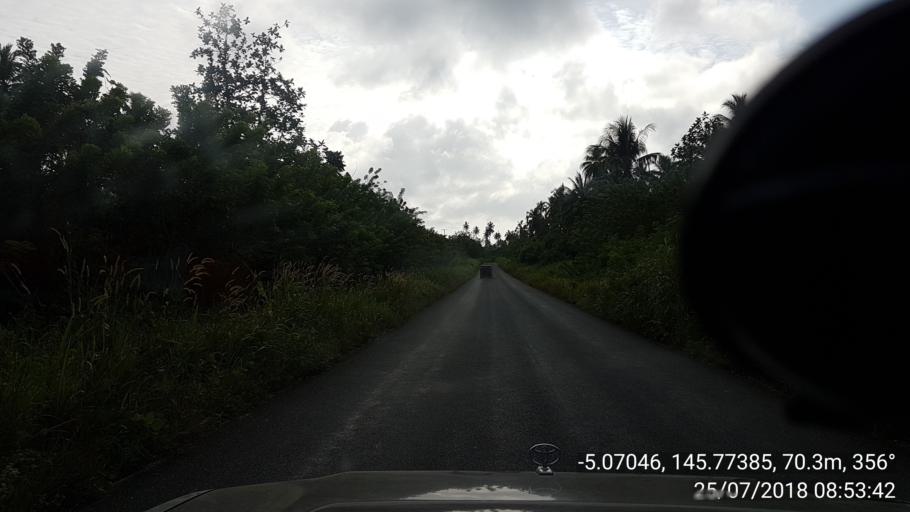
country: PG
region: Madang
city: Madang
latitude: -5.0706
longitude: 145.7737
